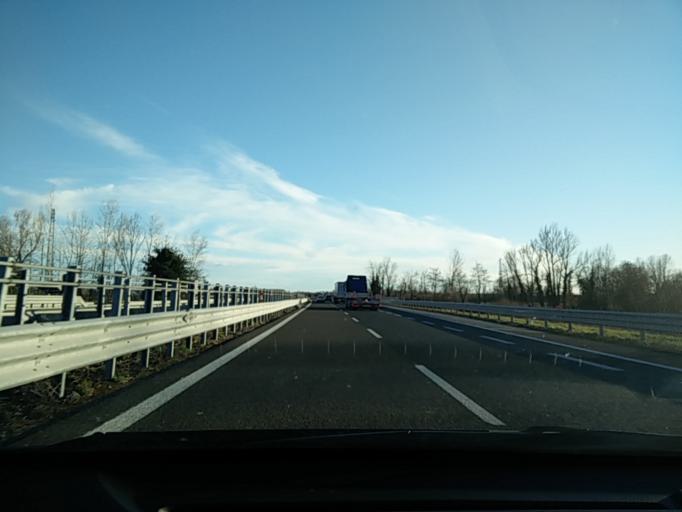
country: IT
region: Friuli Venezia Giulia
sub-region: Provincia di Udine
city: Buia
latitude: 46.2236
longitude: 13.0935
